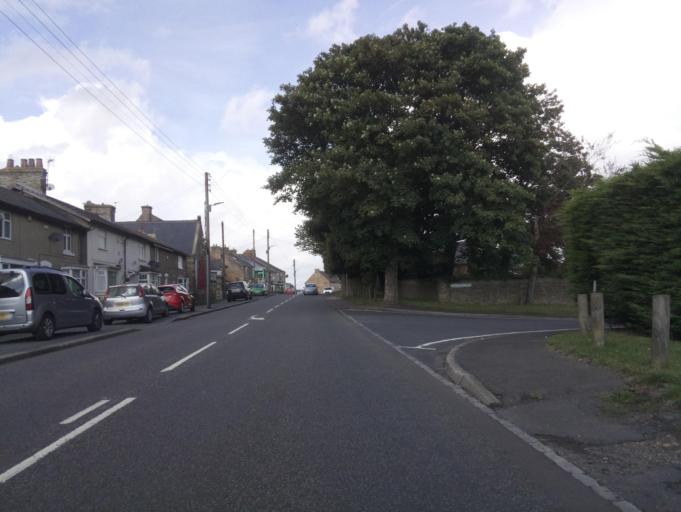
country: GB
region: England
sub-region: County Durham
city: High Etherley
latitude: 54.6471
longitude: -1.7458
